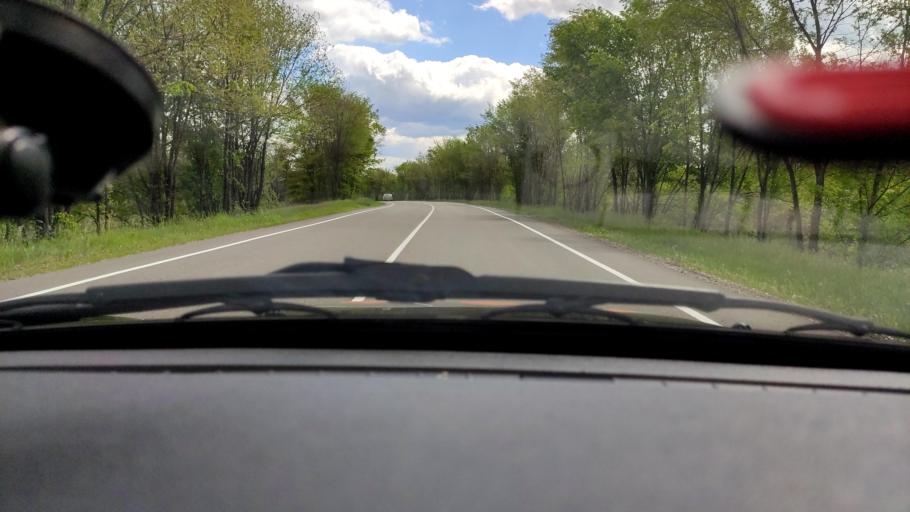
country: RU
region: Belgorod
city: Krasnoye
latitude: 51.0644
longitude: 38.8204
